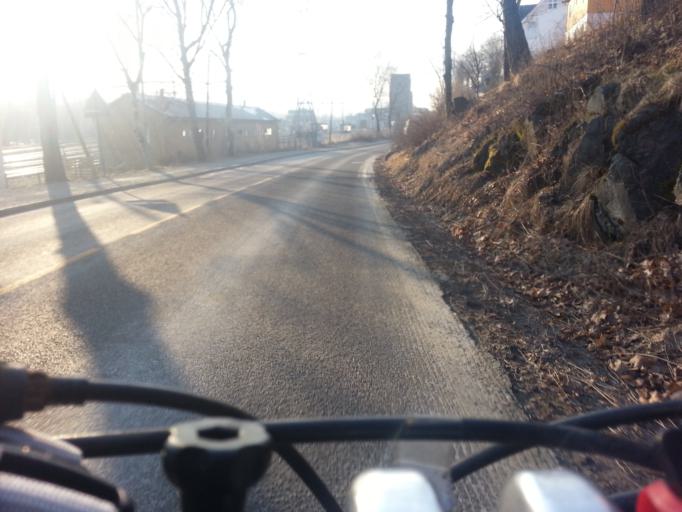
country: NO
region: Sor-Trondelag
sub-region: Trondheim
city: Trondheim
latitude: 63.4246
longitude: 10.3734
